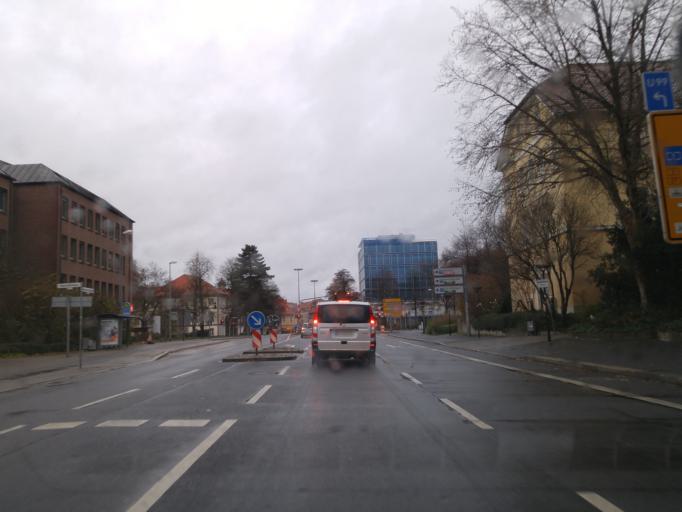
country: DE
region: Lower Saxony
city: Goettingen
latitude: 51.5282
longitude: 9.9390
